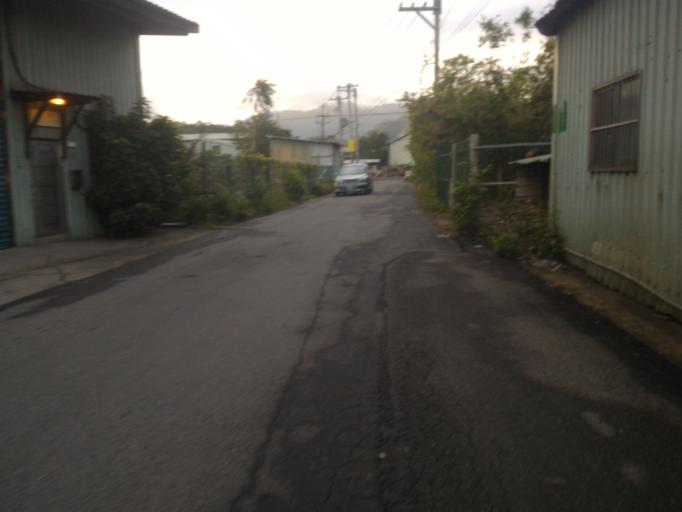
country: TW
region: Taiwan
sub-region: Taoyuan
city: Taoyuan
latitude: 24.9452
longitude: 121.3941
